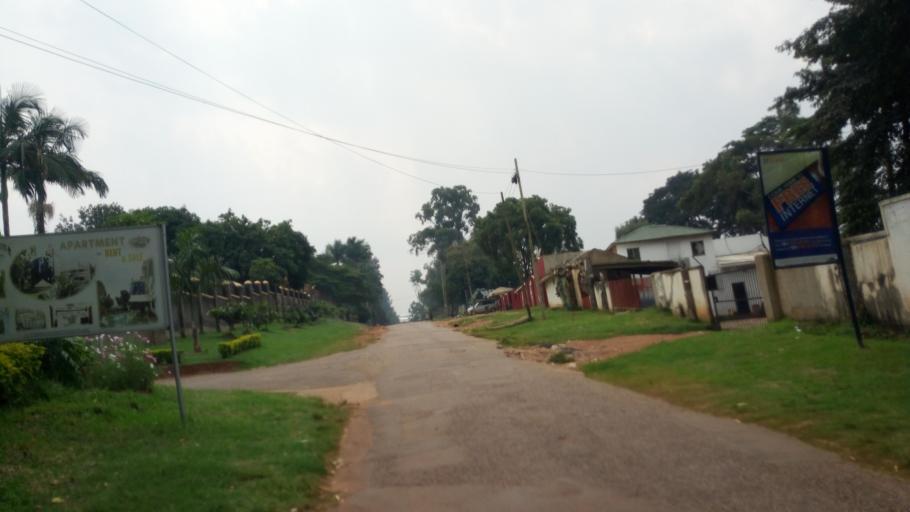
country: UG
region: Central Region
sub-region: Kampala District
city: Kampala
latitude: 0.3104
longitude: 32.6255
